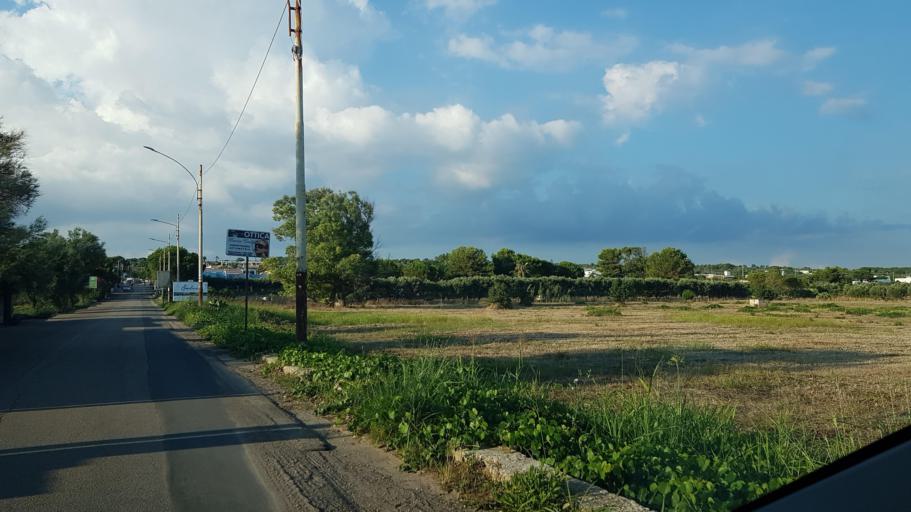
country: IT
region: Apulia
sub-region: Provincia di Lecce
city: Gemini
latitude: 39.8413
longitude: 18.2089
